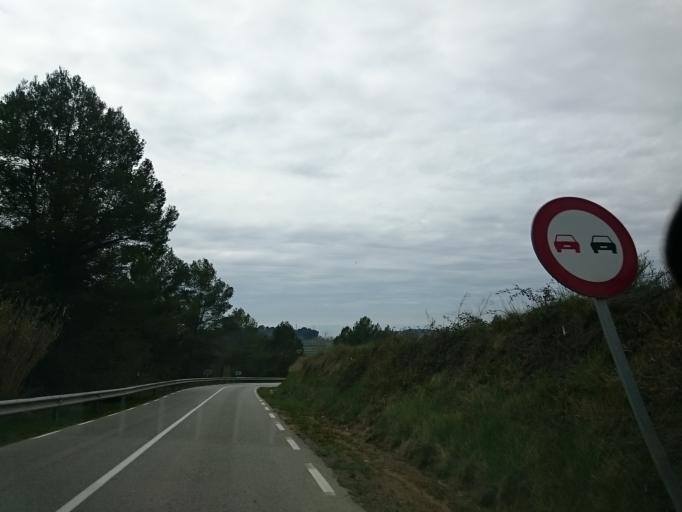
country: ES
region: Catalonia
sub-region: Provincia de Barcelona
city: Sant Sadurni d'Anoia
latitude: 41.4417
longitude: 1.8018
